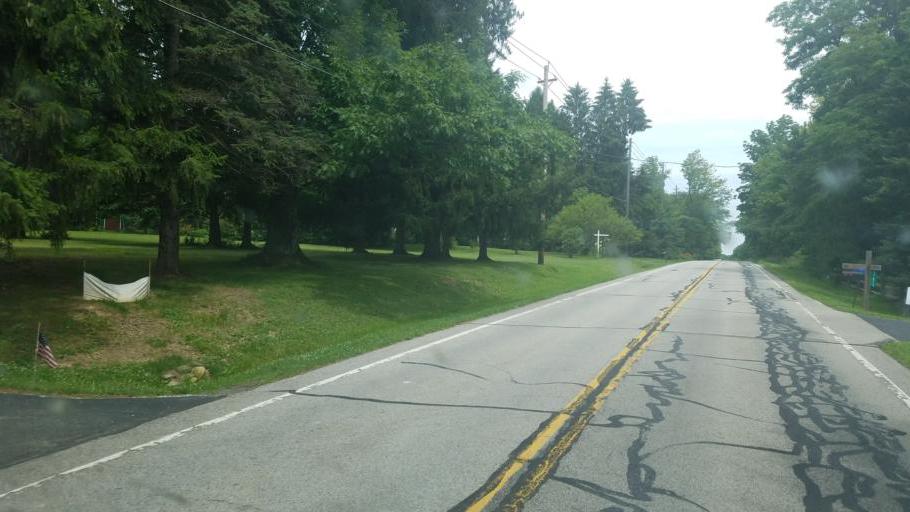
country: US
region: Ohio
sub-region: Geauga County
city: Bainbridge
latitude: 41.3940
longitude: -81.2463
